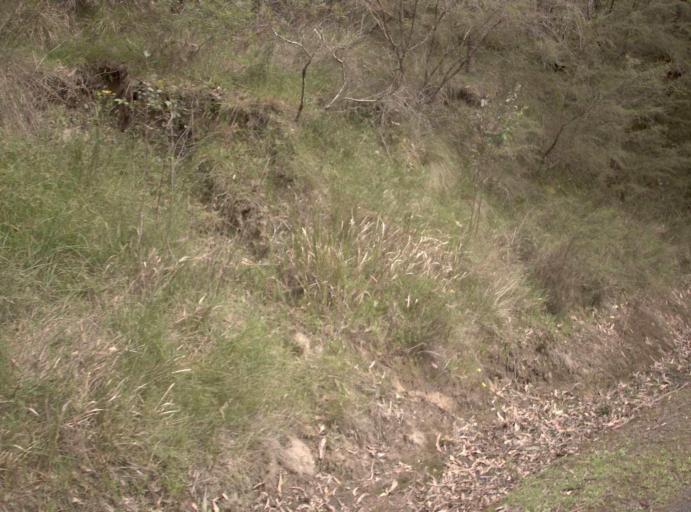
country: AU
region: New South Wales
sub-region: Bombala
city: Bombala
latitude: -37.4259
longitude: 149.1999
